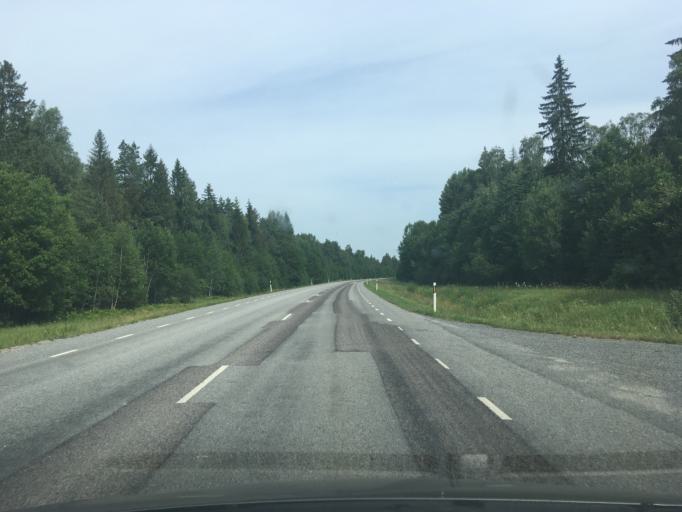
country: EE
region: Raplamaa
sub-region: Rapla vald
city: Rapla
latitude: 59.0077
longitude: 24.7697
